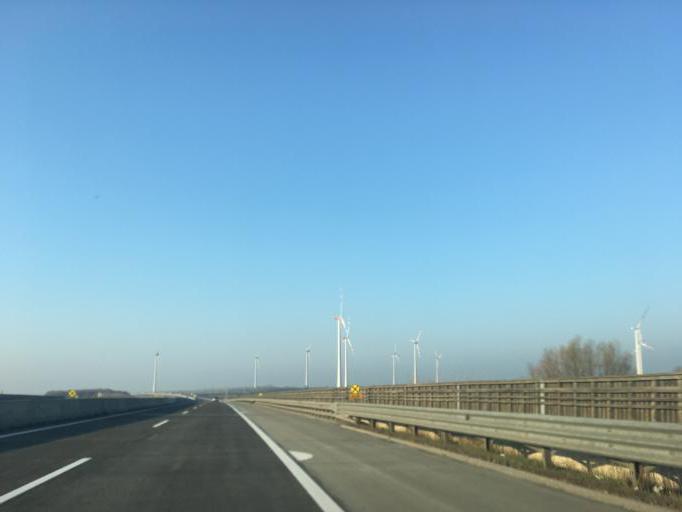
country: AT
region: Burgenland
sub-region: Politischer Bezirk Neusiedl am See
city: Pama
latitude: 48.0617
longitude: 17.0050
